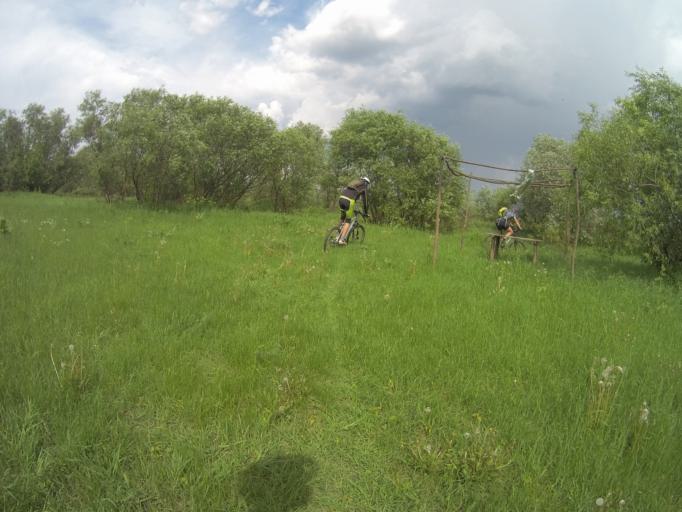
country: RU
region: Vladimir
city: Vorsha
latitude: 56.0366
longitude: 40.1941
